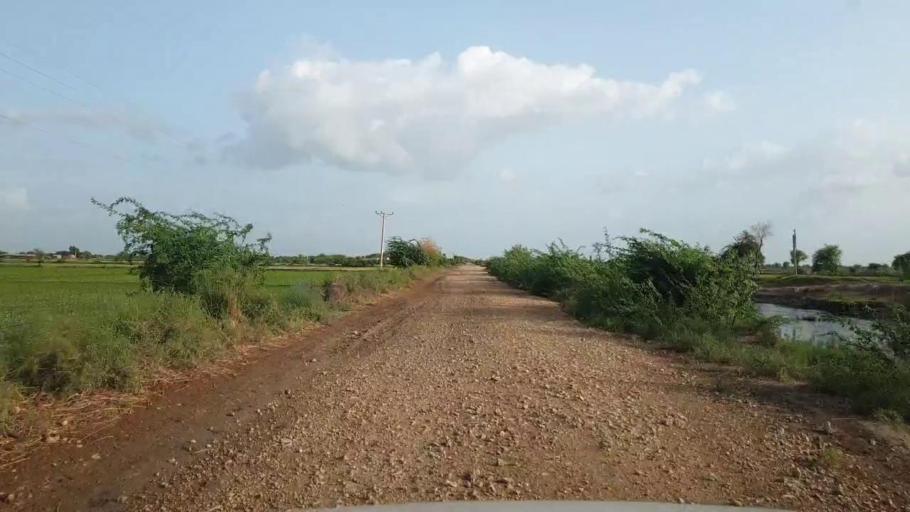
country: PK
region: Sindh
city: Kario
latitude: 24.8163
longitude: 68.6467
